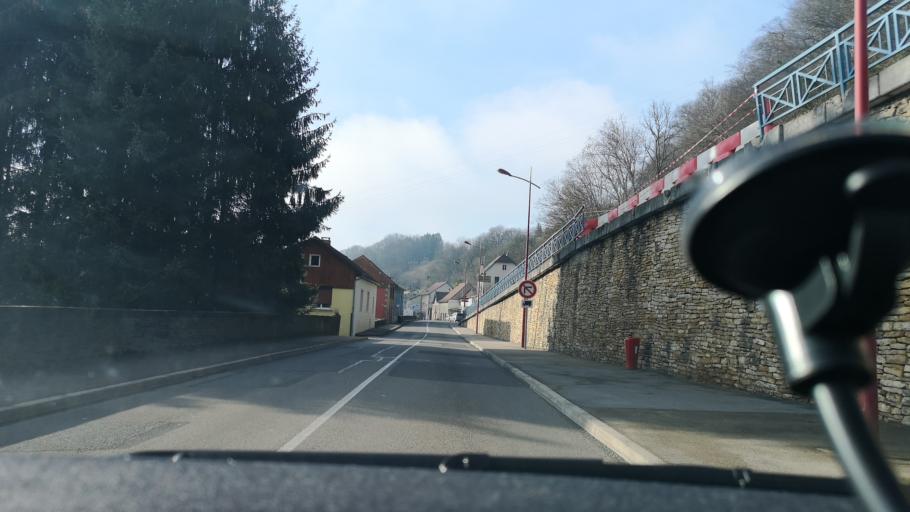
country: FR
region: Franche-Comte
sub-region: Departement du Doubs
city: Montenois
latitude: 47.4546
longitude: 6.5823
